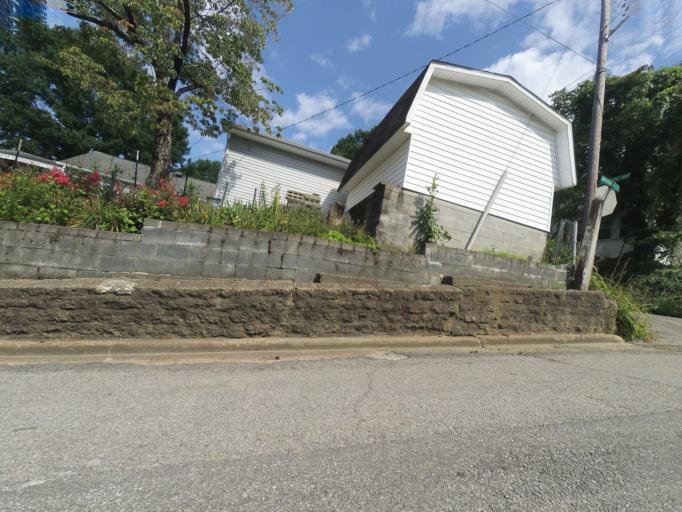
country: US
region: West Virginia
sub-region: Cabell County
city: Huntington
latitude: 38.4109
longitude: -82.4222
